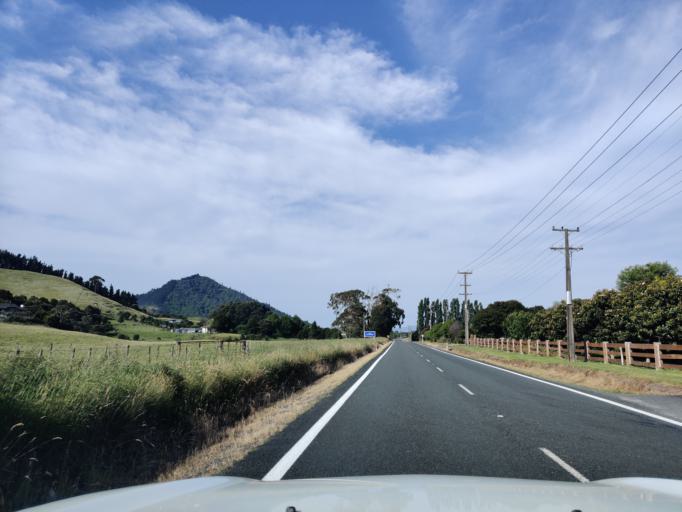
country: NZ
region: Waikato
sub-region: Waikato District
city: Ngaruawahia
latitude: -37.6226
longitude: 175.1747
